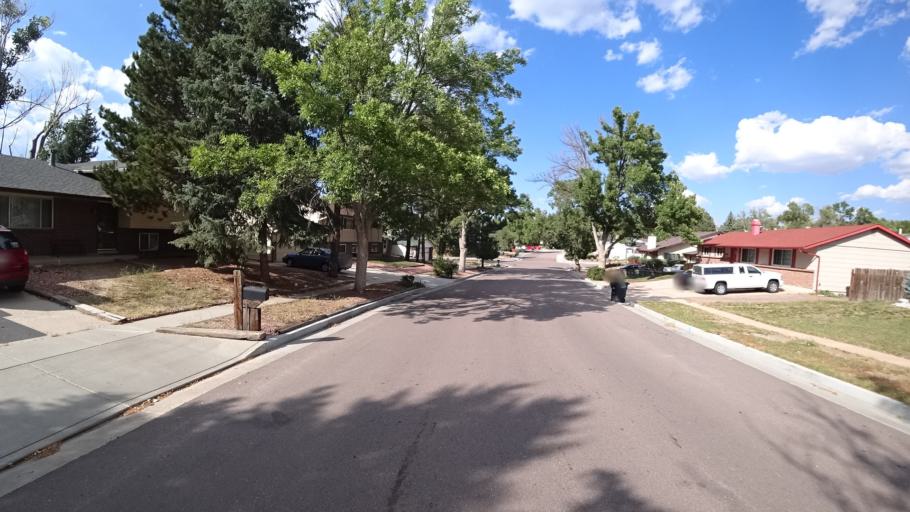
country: US
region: Colorado
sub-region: El Paso County
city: Cimarron Hills
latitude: 38.8771
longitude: -104.7342
